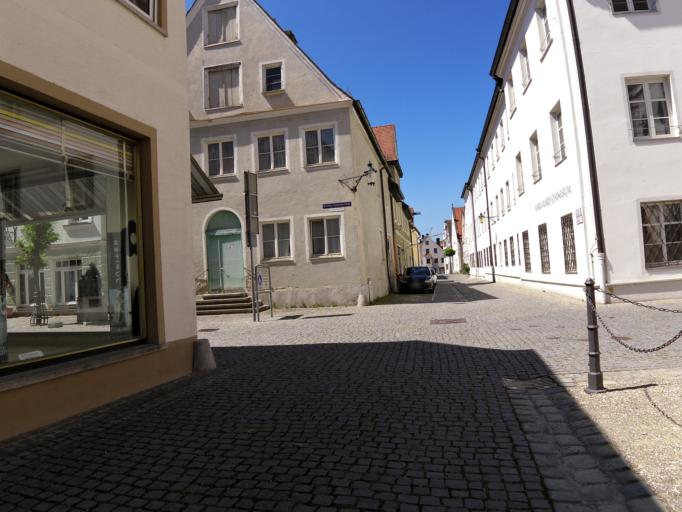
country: DE
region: Bavaria
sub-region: Swabia
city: Guenzburg
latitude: 48.4565
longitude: 10.2768
